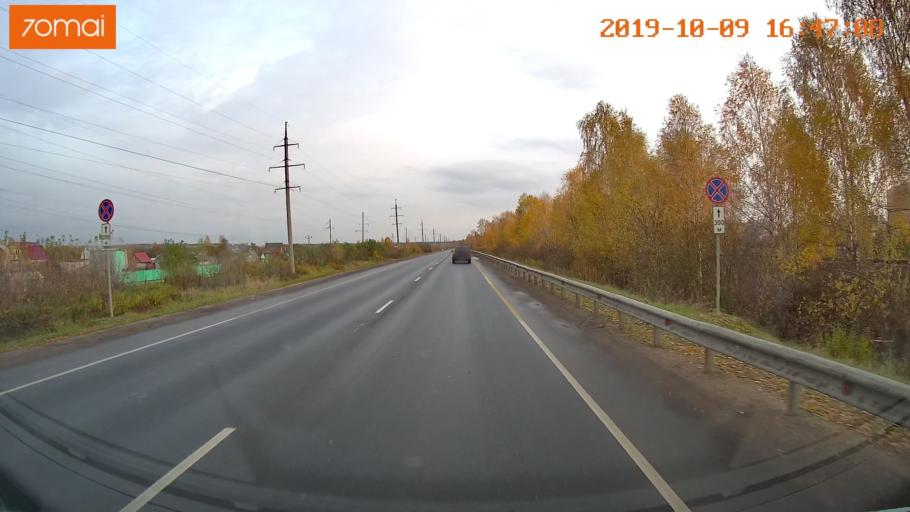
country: RU
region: Kostroma
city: Volgorechensk
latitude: 57.4392
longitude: 41.1733
